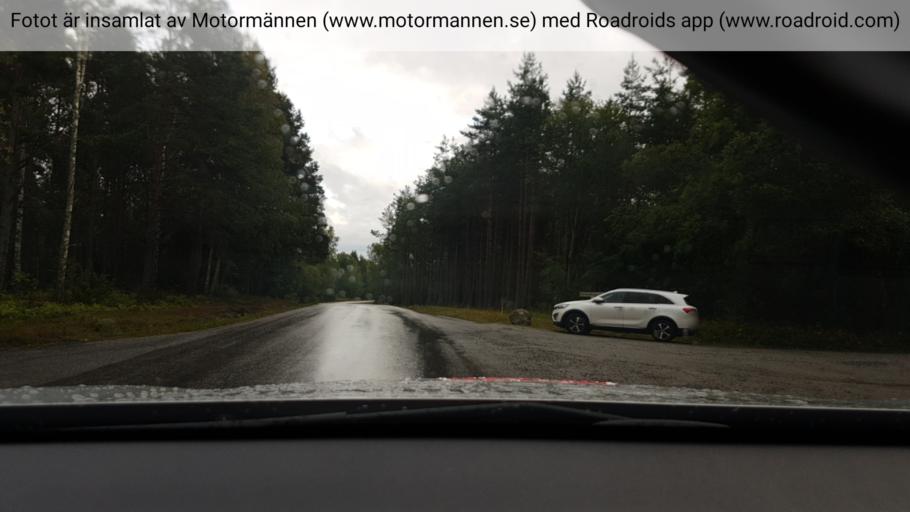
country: SE
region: Stockholm
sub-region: Haninge Kommun
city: Jordbro
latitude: 59.0862
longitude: 18.0471
